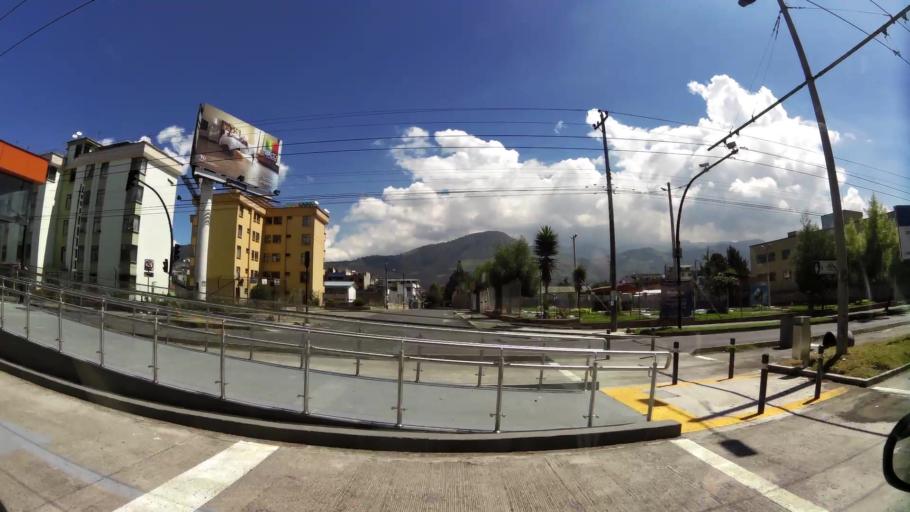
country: EC
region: Pichincha
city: Quito
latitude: -0.2699
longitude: -78.5351
